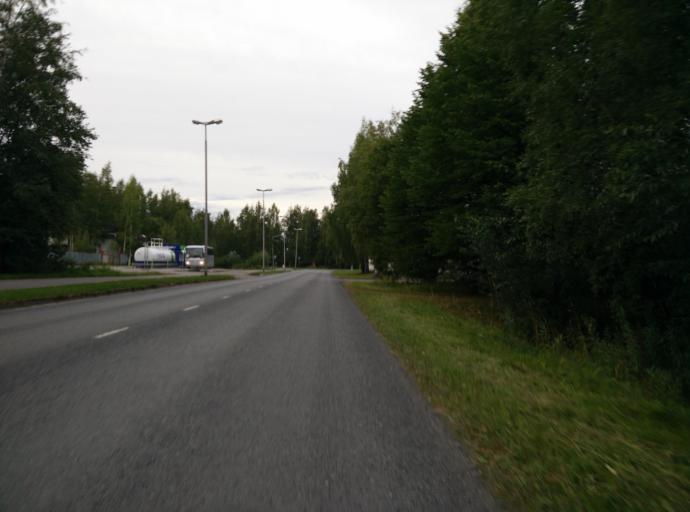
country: FI
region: Haeme
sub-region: Haemeenlinna
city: Haemeenlinna
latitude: 60.9934
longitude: 24.4851
